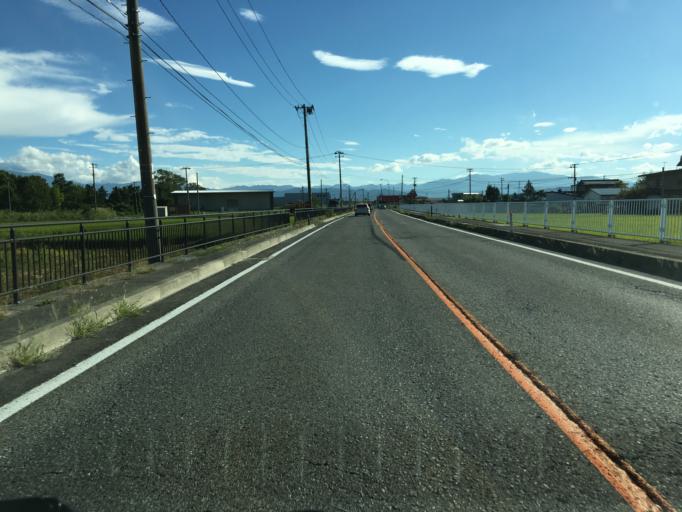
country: JP
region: Yamagata
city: Takahata
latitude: 37.9776
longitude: 140.1356
